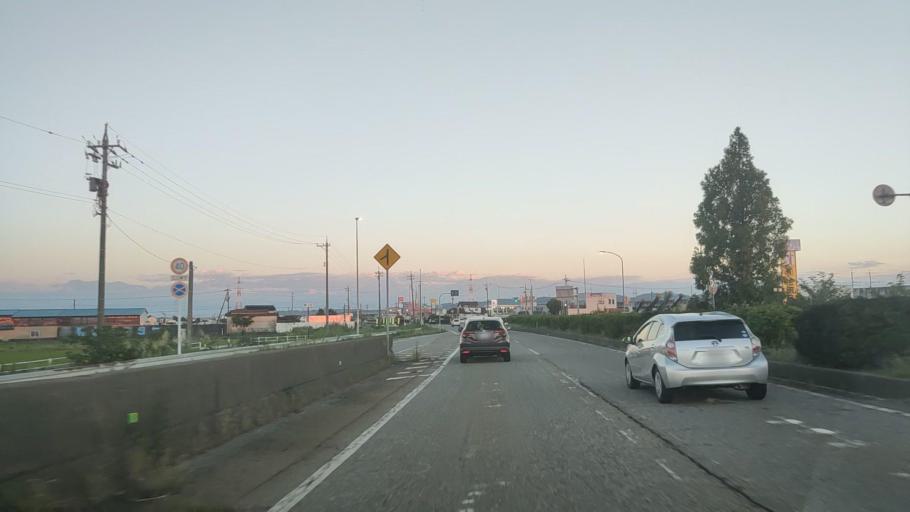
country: JP
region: Toyama
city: Kuragaki-kosugi
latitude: 36.7283
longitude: 137.1257
